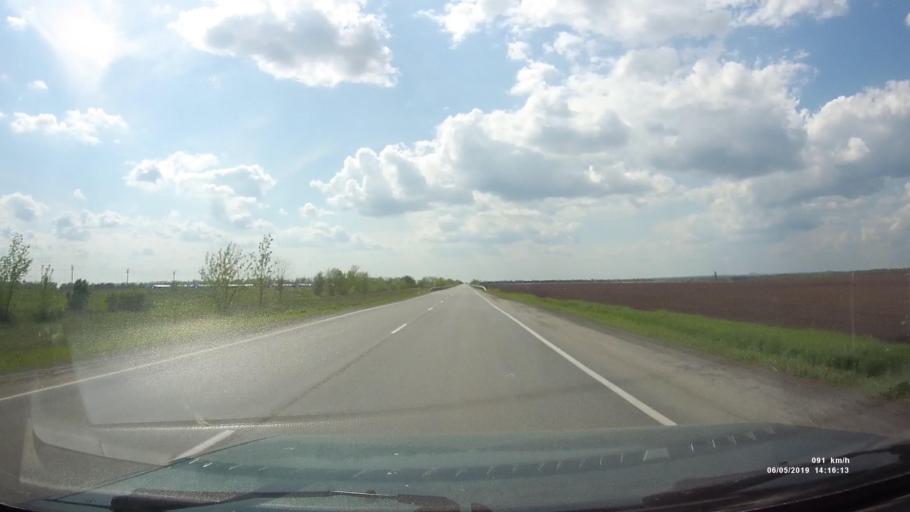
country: RU
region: Rostov
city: Kamenolomni
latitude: 47.6349
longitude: 40.2921
